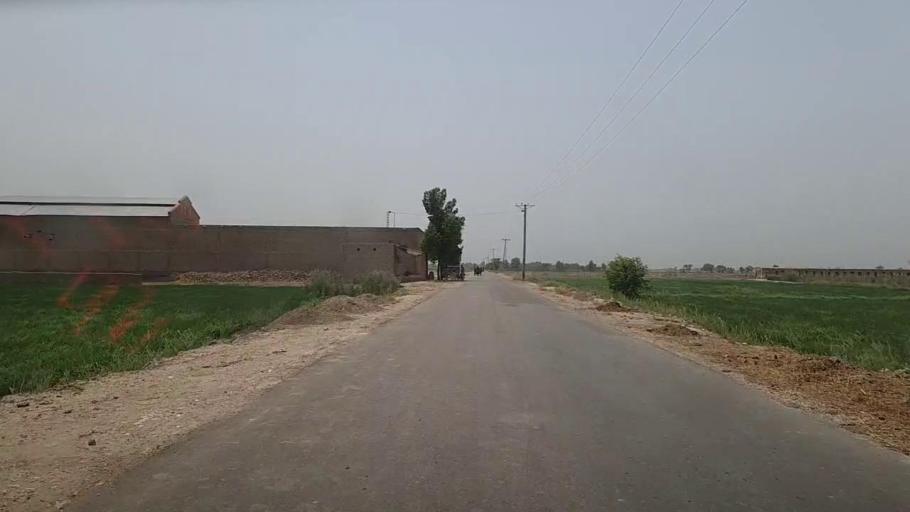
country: PK
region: Sindh
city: Sita Road
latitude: 27.0531
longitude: 67.9024
